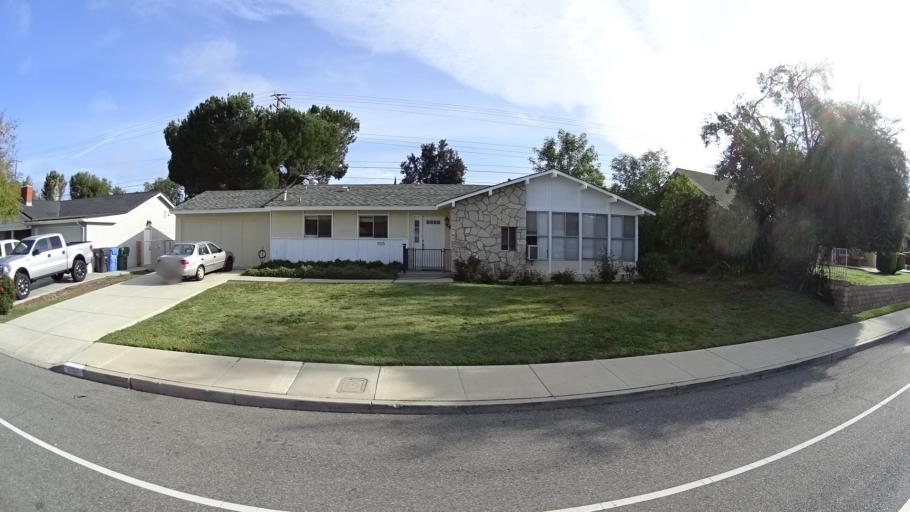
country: US
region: California
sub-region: Ventura County
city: Thousand Oaks
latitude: 34.2156
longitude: -118.8620
